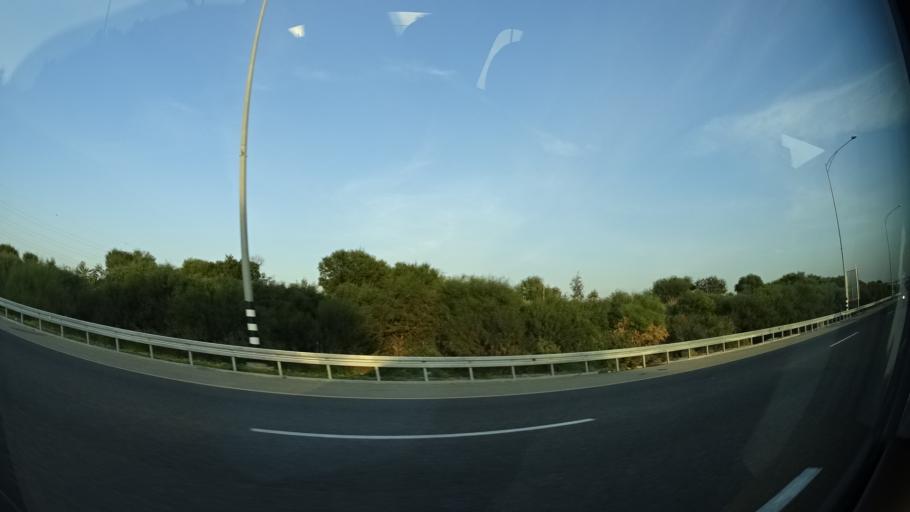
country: IL
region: Central District
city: Kefar Habad
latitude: 31.9933
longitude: 34.8564
